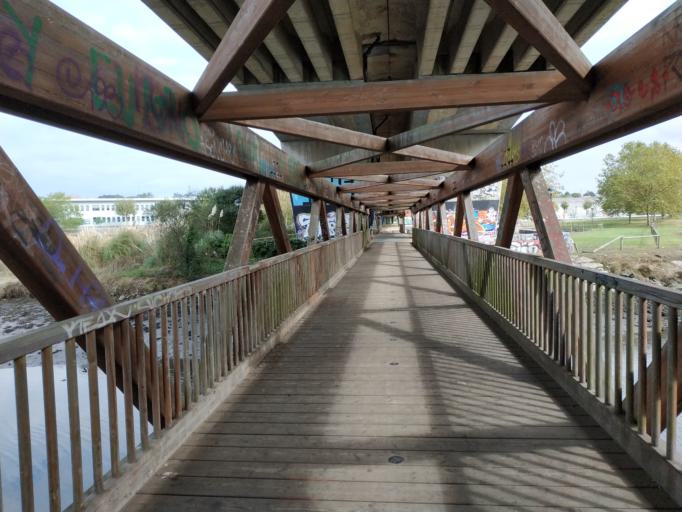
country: ES
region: Galicia
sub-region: Provincia da Coruna
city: Cambre
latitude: 43.3125
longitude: -8.3585
